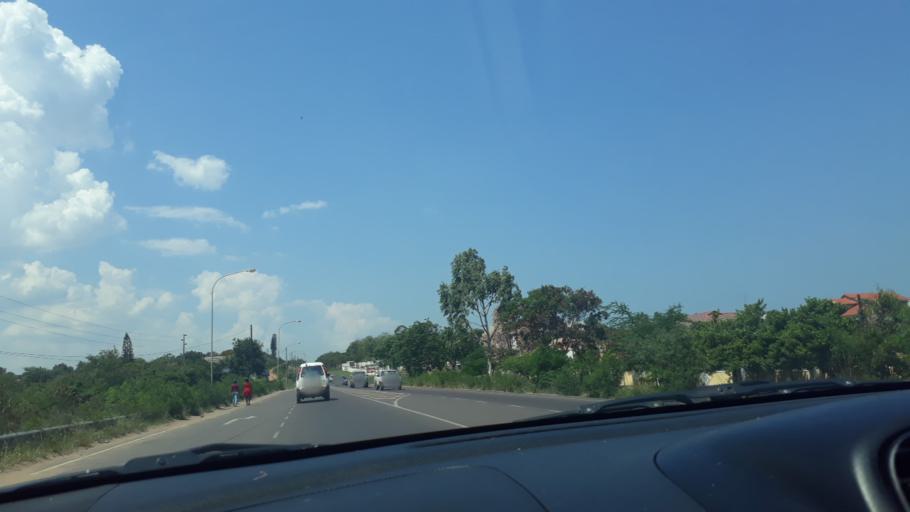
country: MZ
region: Maputo
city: Matola
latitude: -25.9669
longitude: 32.4443
